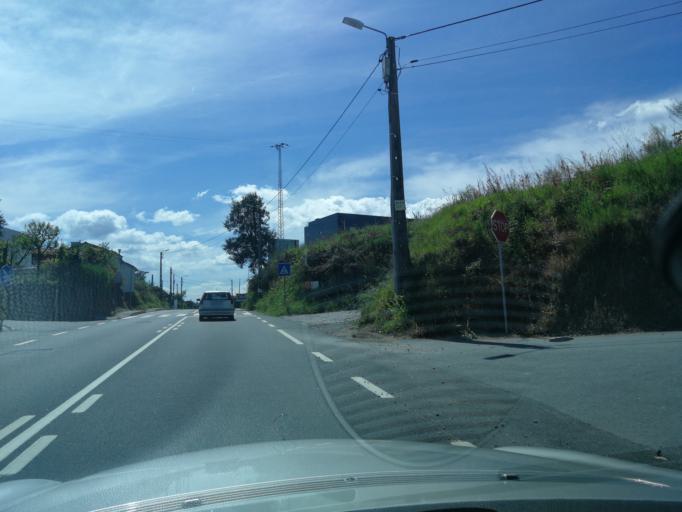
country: PT
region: Braga
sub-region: Vila Nova de Famalicao
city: Calendario
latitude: 41.4187
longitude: -8.5344
